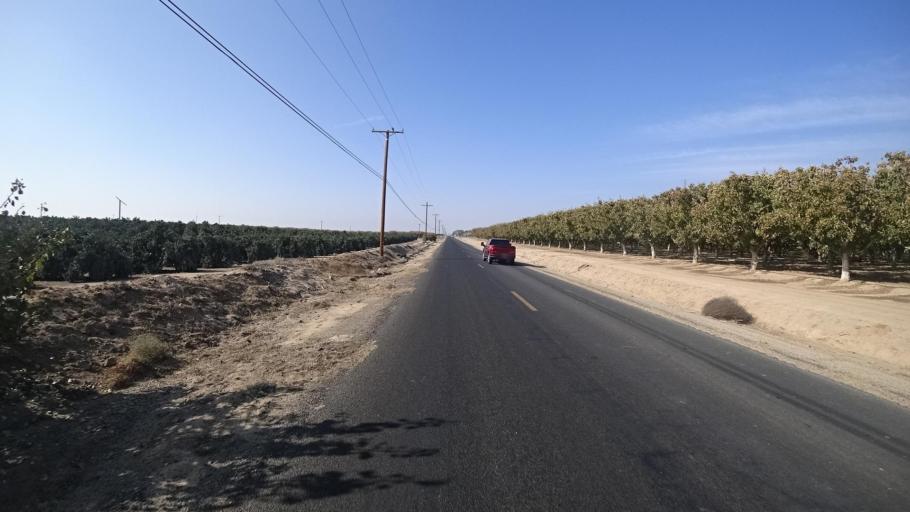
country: US
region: California
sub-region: Kern County
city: McFarland
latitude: 35.6746
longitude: -119.1626
